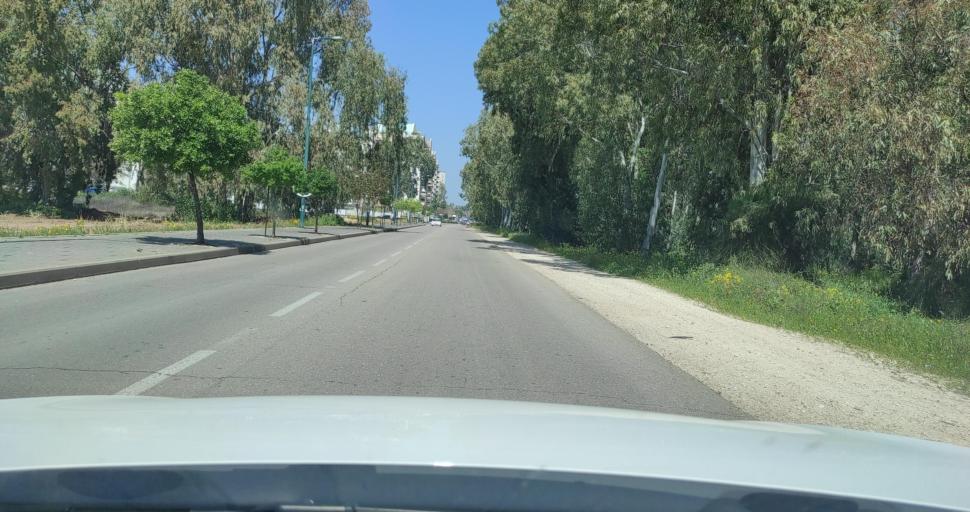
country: IL
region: Central District
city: Nordiyya
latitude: 32.3049
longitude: 34.8741
